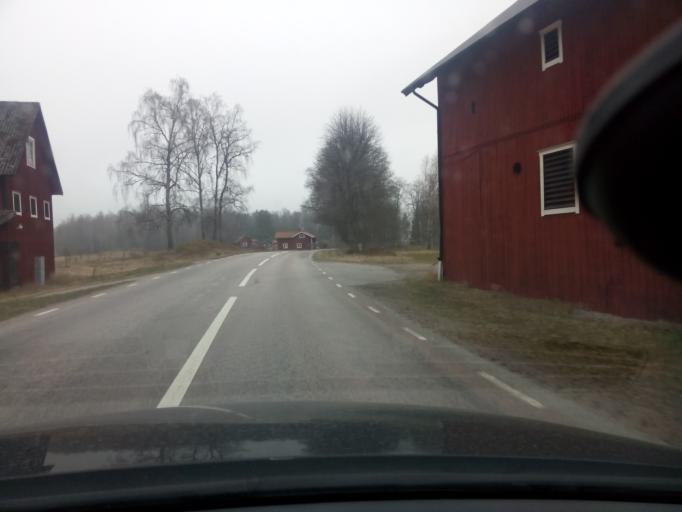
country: SE
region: Soedermanland
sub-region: Gnesta Kommun
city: Gnesta
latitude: 58.9521
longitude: 17.1271
